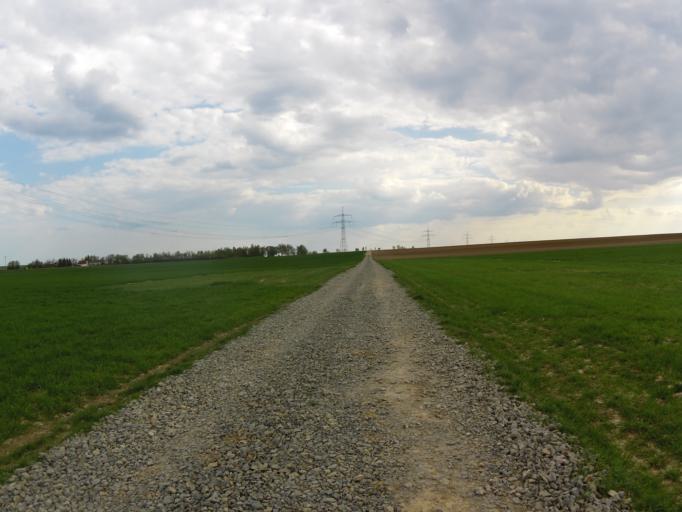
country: DE
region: Bavaria
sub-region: Regierungsbezirk Unterfranken
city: Oberpleichfeld
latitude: 49.8615
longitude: 10.0947
